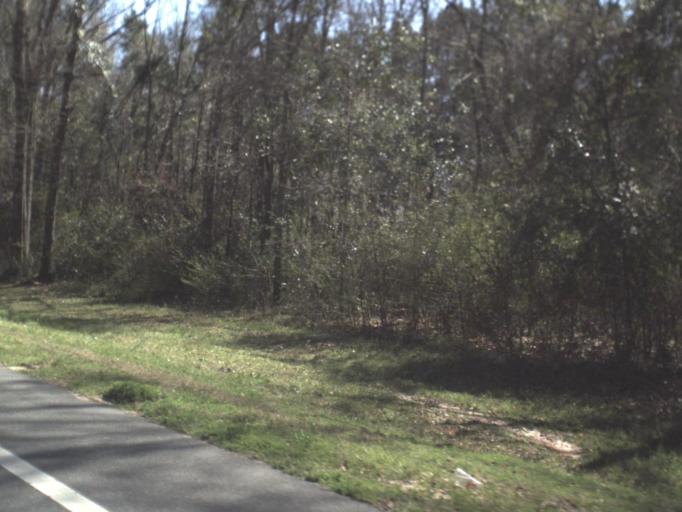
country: US
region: Florida
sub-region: Gadsden County
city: Gretna
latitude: 30.5938
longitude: -84.6463
